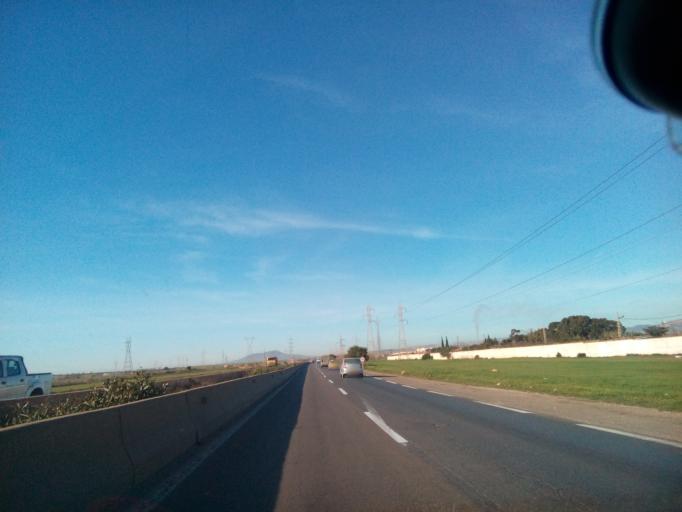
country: DZ
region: Oran
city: Ain el Bya
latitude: 35.8017
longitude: -0.3043
